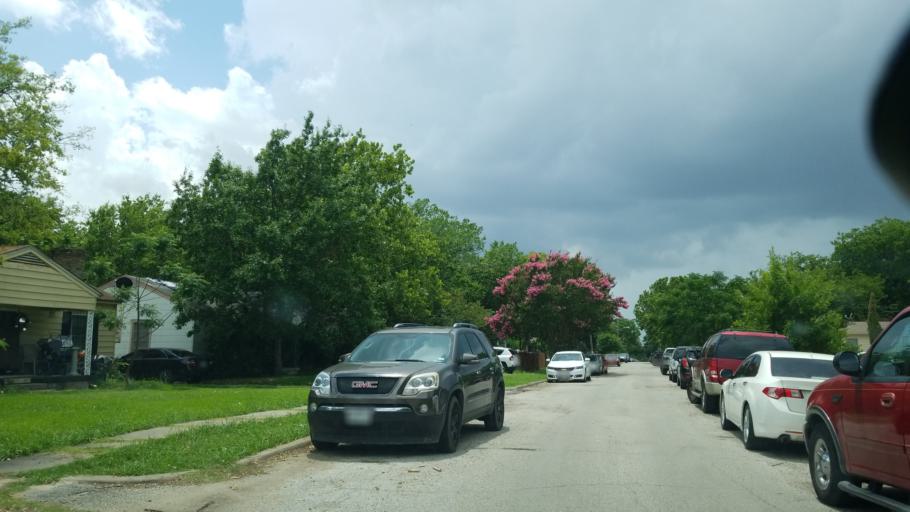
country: US
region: Texas
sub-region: Dallas County
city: Farmers Branch
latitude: 32.8734
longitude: -96.8621
